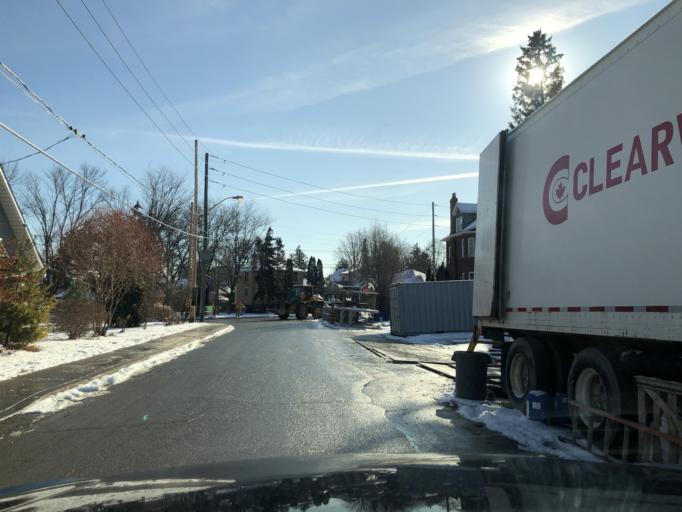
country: CA
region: Ontario
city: Etobicoke
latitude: 43.7070
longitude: -79.5171
